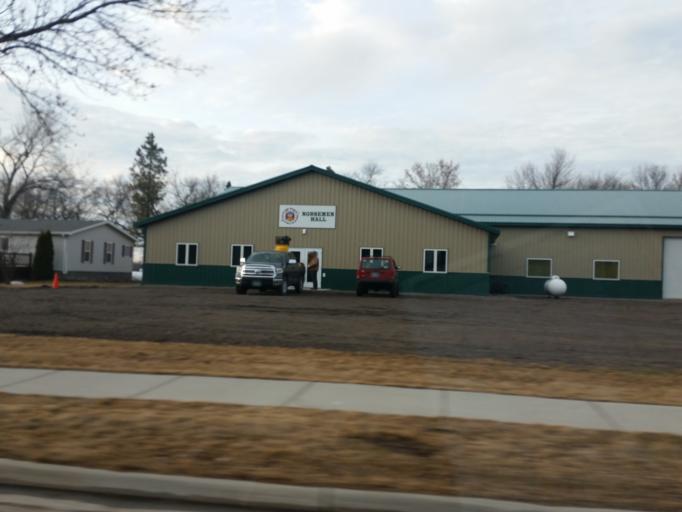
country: US
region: North Dakota
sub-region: Traill County
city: Mayville
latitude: 47.4985
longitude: -97.3775
